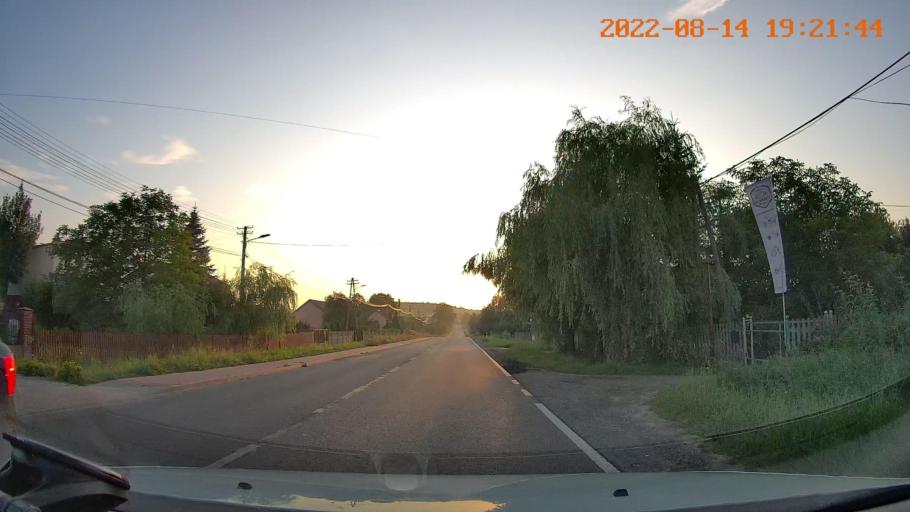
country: PL
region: Swietokrzyskie
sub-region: Powiat kielecki
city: Piekoszow
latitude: 50.8593
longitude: 20.4912
